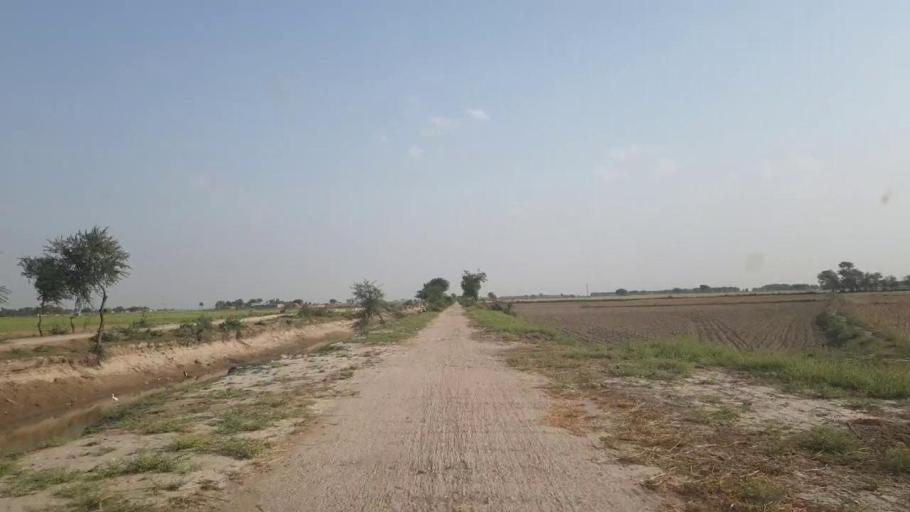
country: PK
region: Sindh
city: Kario
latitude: 24.5994
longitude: 68.5522
